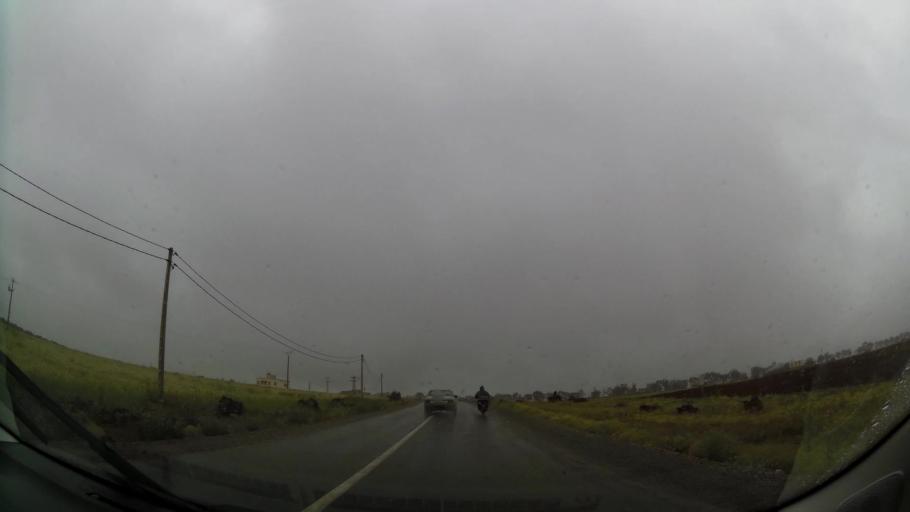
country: MA
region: Oriental
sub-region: Nador
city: Boudinar
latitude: 35.1340
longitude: -3.6248
